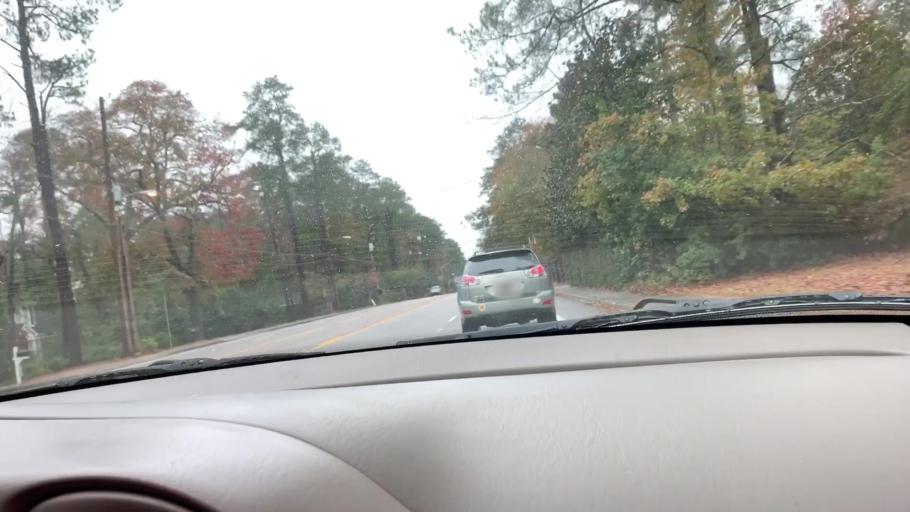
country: US
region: South Carolina
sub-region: Richland County
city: Forest Acres
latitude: 34.0280
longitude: -80.9664
